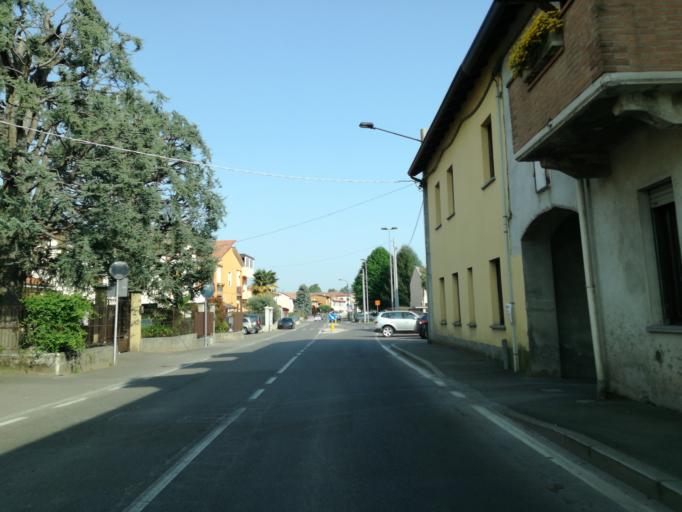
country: IT
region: Lombardy
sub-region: Provincia di Lecco
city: Verderio Inferiore
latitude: 45.6627
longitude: 9.4306
